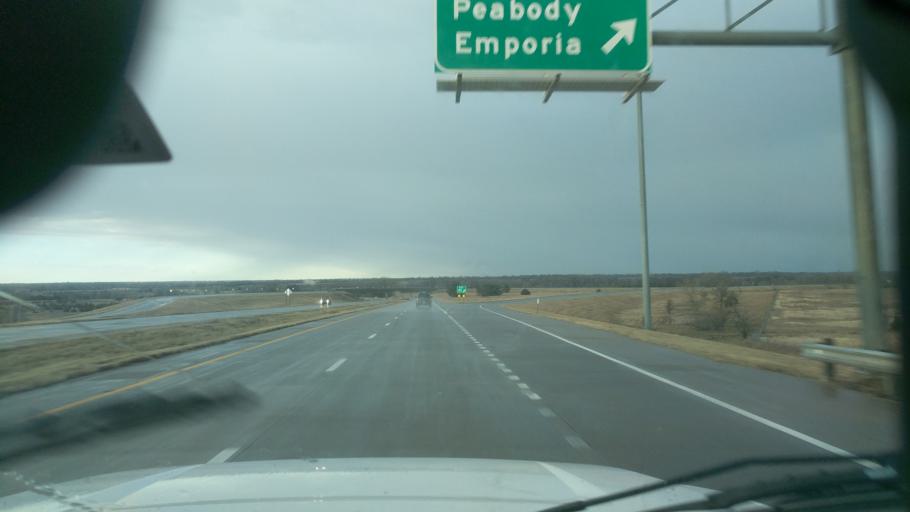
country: US
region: Kansas
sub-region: Harvey County
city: North Newton
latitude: 38.0609
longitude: -97.3225
